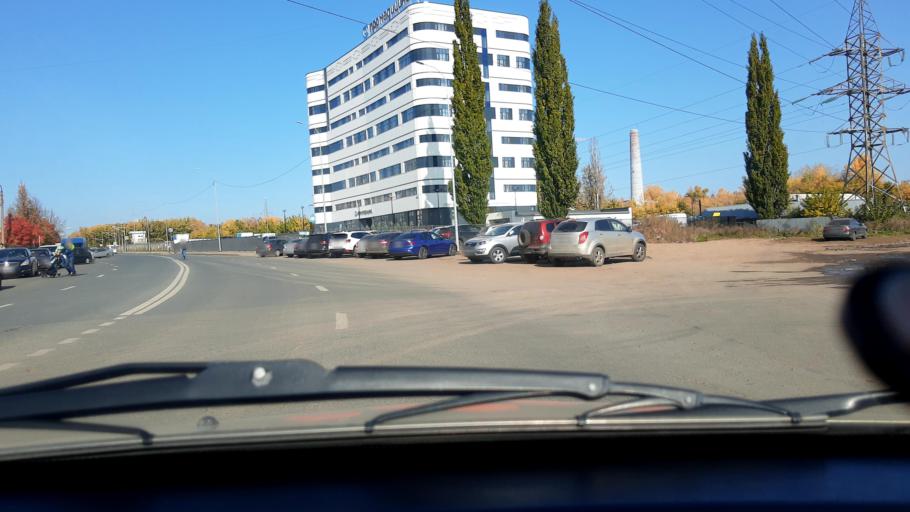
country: RU
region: Bashkortostan
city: Ufa
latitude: 54.7086
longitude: 56.0095
